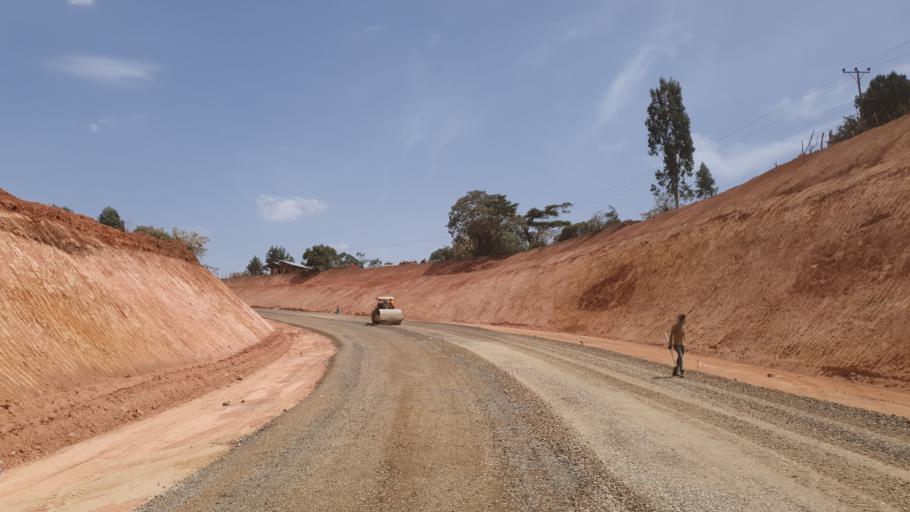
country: ET
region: Oromiya
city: Shambu
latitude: 9.8487
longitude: 36.6404
